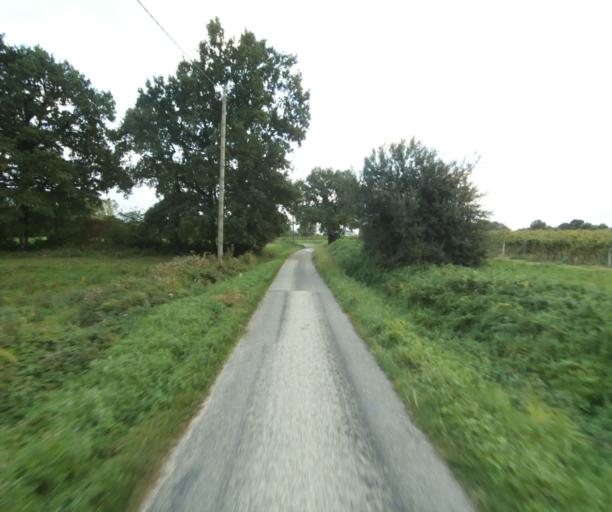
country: FR
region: Aquitaine
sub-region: Departement des Landes
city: Gabarret
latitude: 43.9793
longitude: 0.1033
